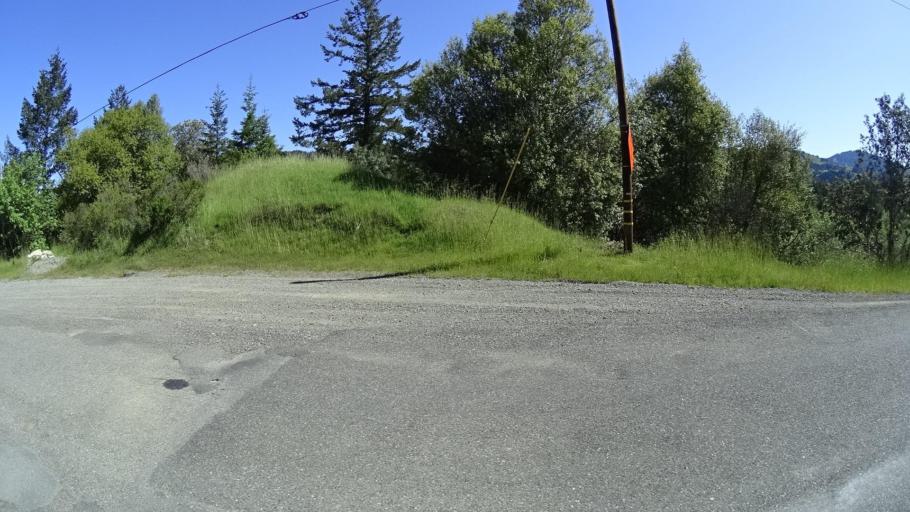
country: US
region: California
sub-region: Humboldt County
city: Rio Dell
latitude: 40.2525
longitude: -124.1881
